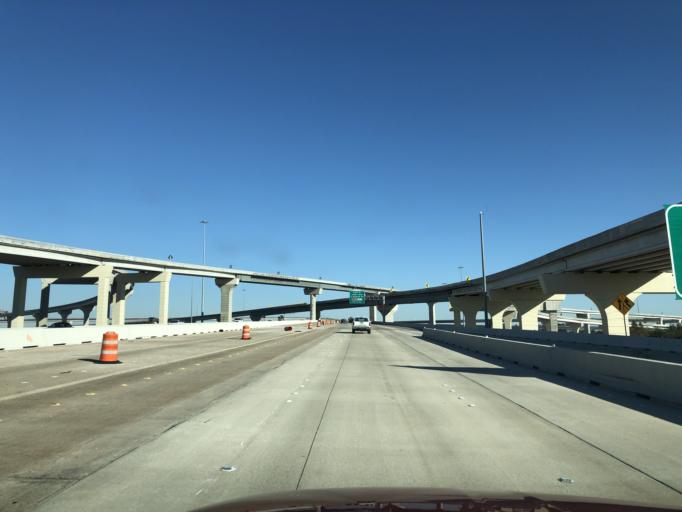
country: US
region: Texas
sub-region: Brazoria County
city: Brookside Village
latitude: 29.5970
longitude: -95.3925
